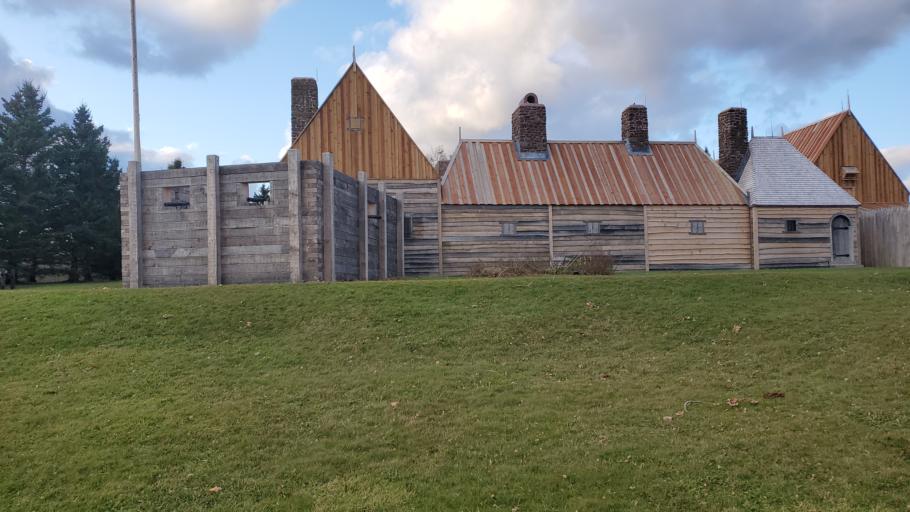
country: CA
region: Nova Scotia
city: Digby
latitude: 44.7110
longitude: -65.6095
